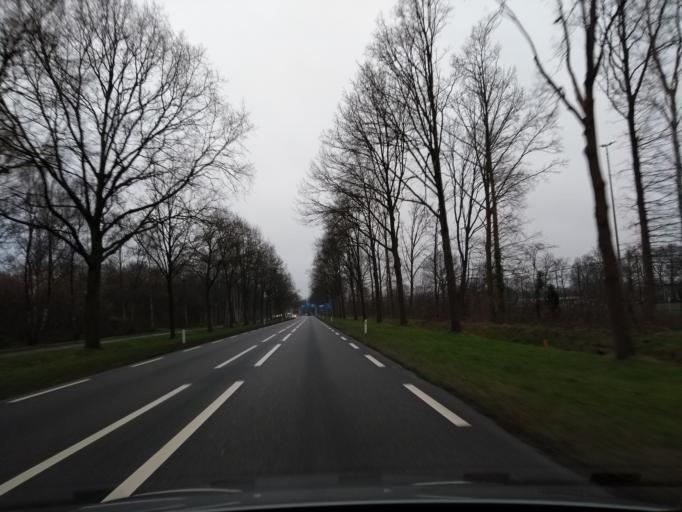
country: NL
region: Overijssel
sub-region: Gemeente Almelo
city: Almelo
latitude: 52.3730
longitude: 6.6698
